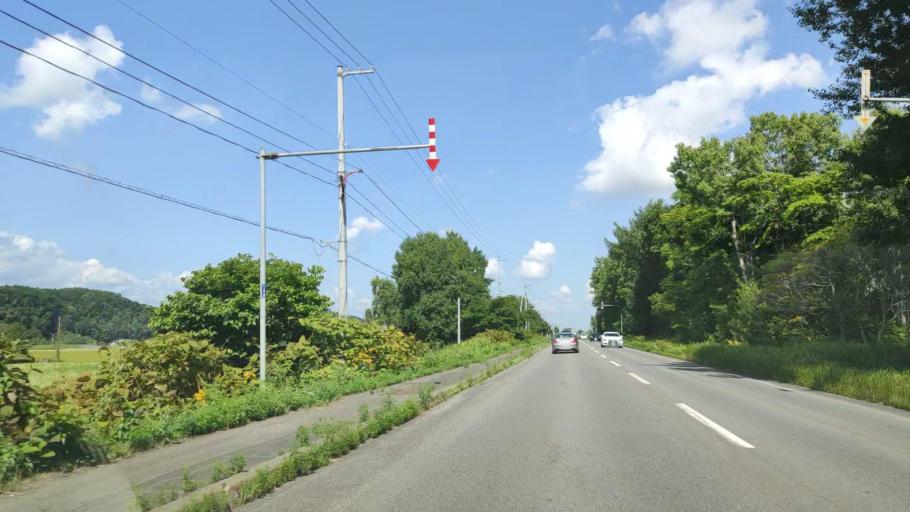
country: JP
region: Hokkaido
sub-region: Asahikawa-shi
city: Asahikawa
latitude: 43.6334
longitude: 142.4577
